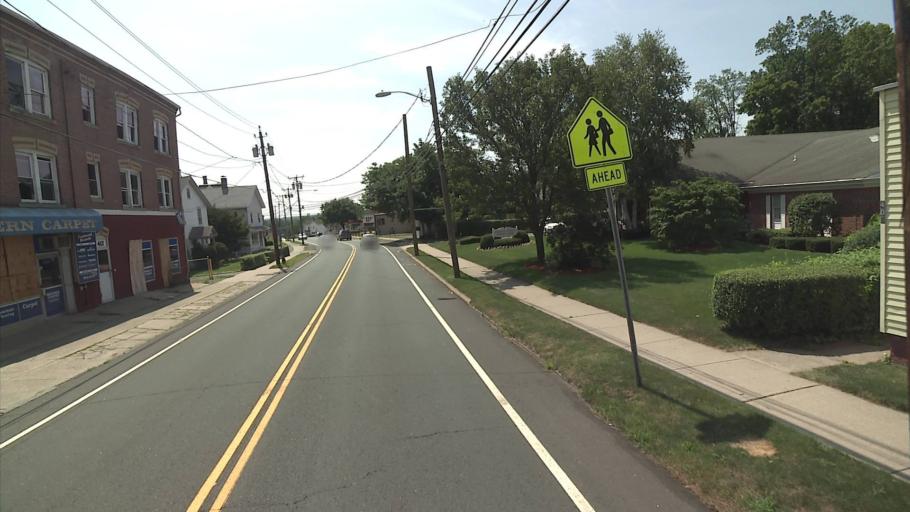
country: US
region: Connecticut
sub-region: Hartford County
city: New Britain
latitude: 41.6538
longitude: -72.7755
